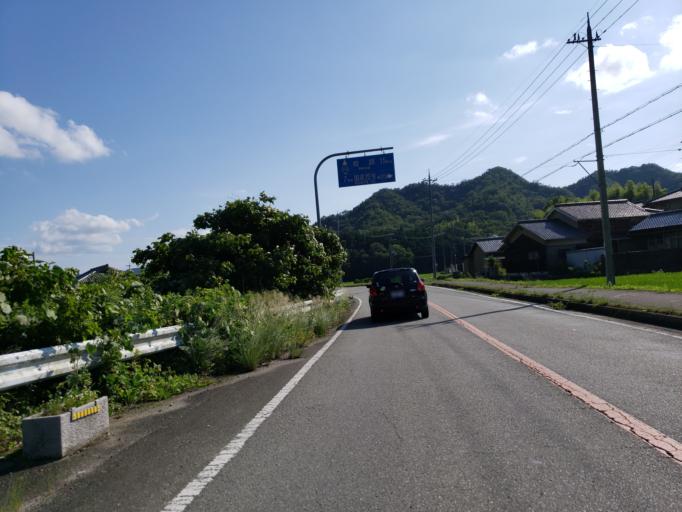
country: JP
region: Hyogo
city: Kakogawacho-honmachi
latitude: 34.8787
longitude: 134.7990
